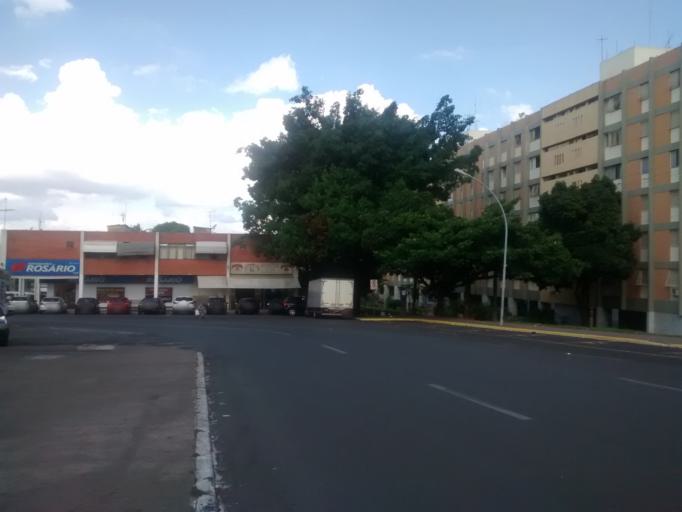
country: BR
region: Federal District
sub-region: Brasilia
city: Brasilia
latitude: -15.7509
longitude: -47.8943
